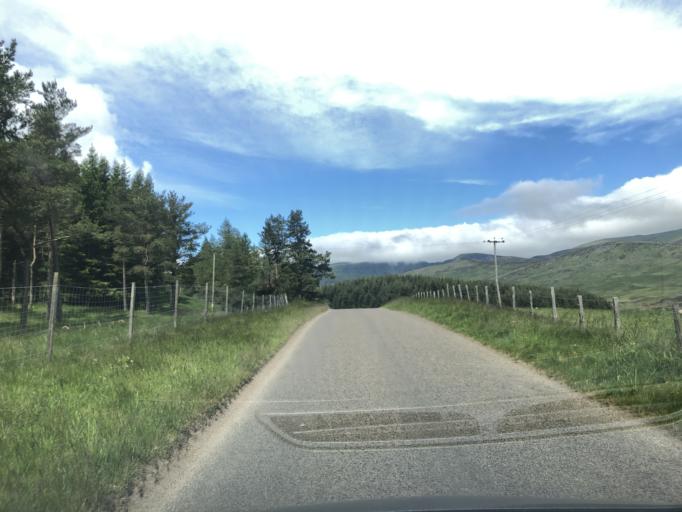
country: GB
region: Scotland
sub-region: Angus
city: Kirriemuir
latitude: 56.8223
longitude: -3.0613
